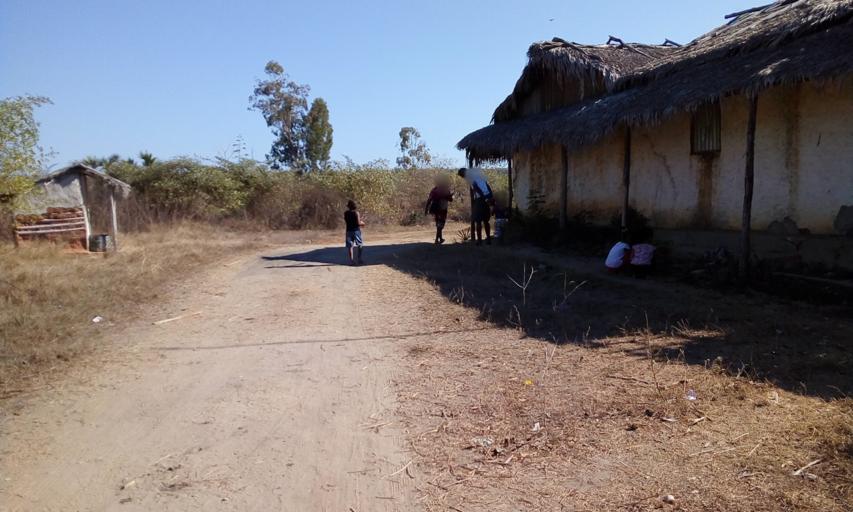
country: MG
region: Boeny
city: Mahajanga
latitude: -15.6257
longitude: 46.4192
